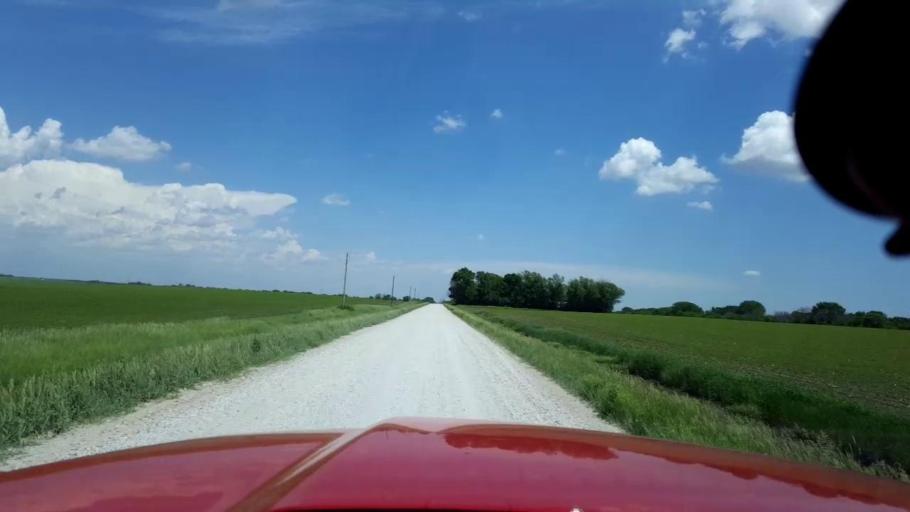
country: US
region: Iowa
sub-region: Boone County
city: Boone
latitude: 42.0493
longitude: -93.7738
